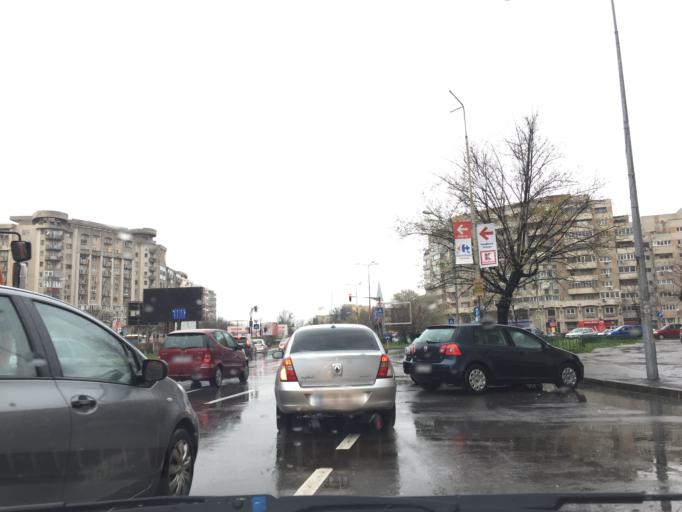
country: RO
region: Bucuresti
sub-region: Municipiul Bucuresti
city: Bucuresti
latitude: 44.4228
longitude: 26.0739
